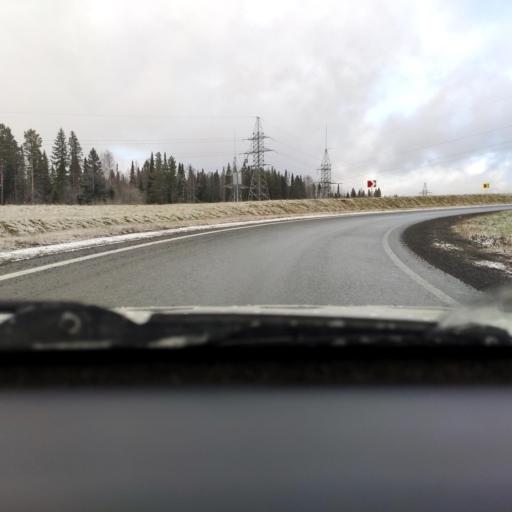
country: RU
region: Perm
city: Perm
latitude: 58.0454
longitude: 56.4279
